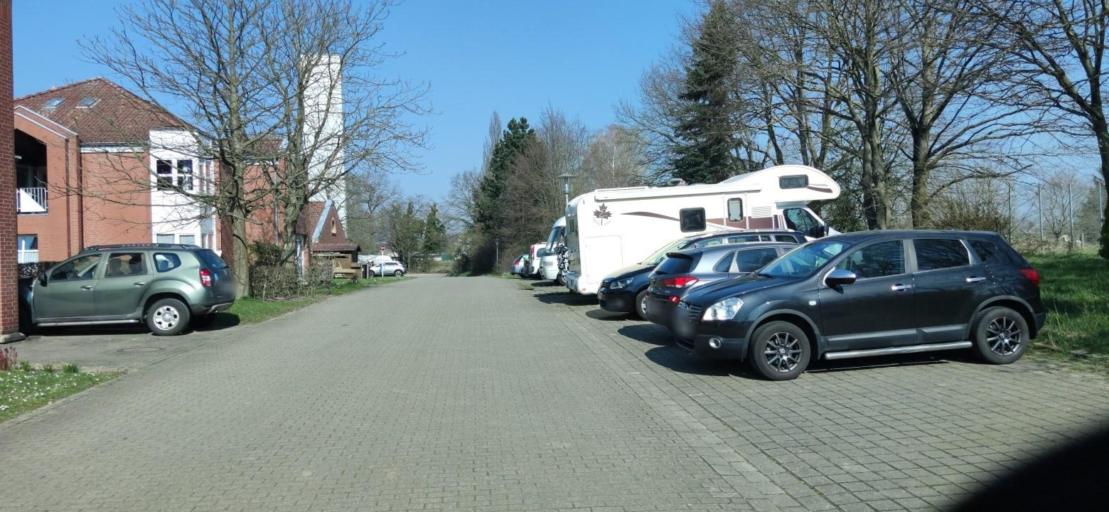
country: DE
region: North Rhine-Westphalia
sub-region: Regierungsbezirk Dusseldorf
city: Muelheim (Ruhr)
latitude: 51.3743
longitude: 6.8579
